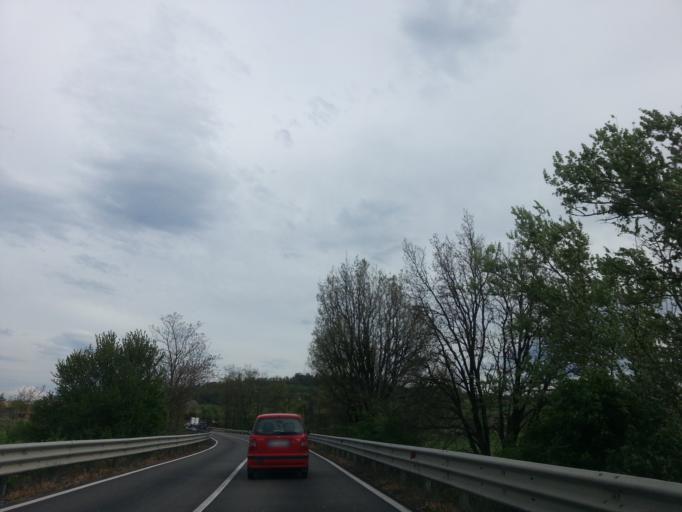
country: IT
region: Emilia-Romagna
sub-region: Provincia di Reggio Emilia
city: Puianello
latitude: 44.6237
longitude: 10.5687
